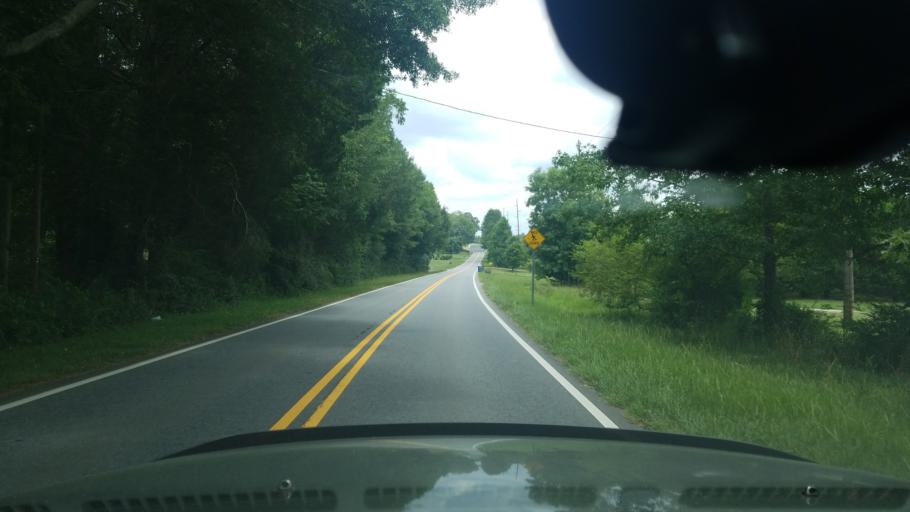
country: US
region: Georgia
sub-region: Forsyth County
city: Cumming
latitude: 34.1969
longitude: -84.2036
